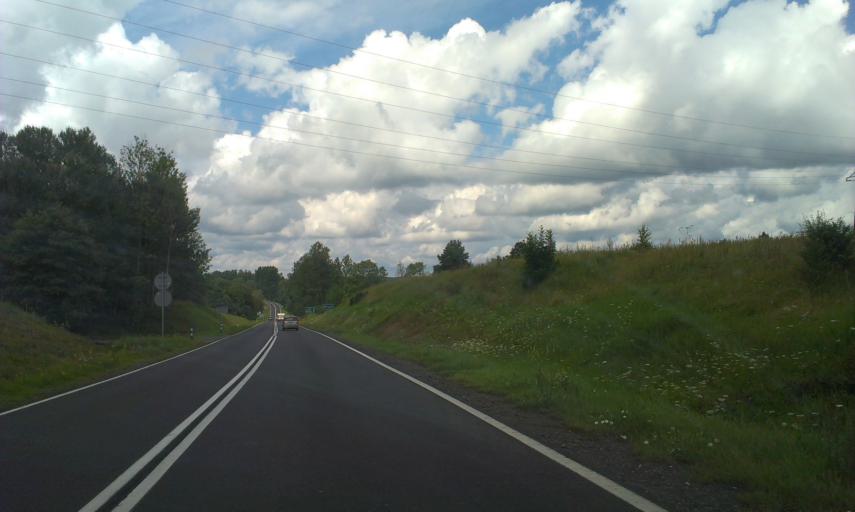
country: PL
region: West Pomeranian Voivodeship
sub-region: Powiat koszalinski
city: Bobolice
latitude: 53.9640
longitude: 16.5780
